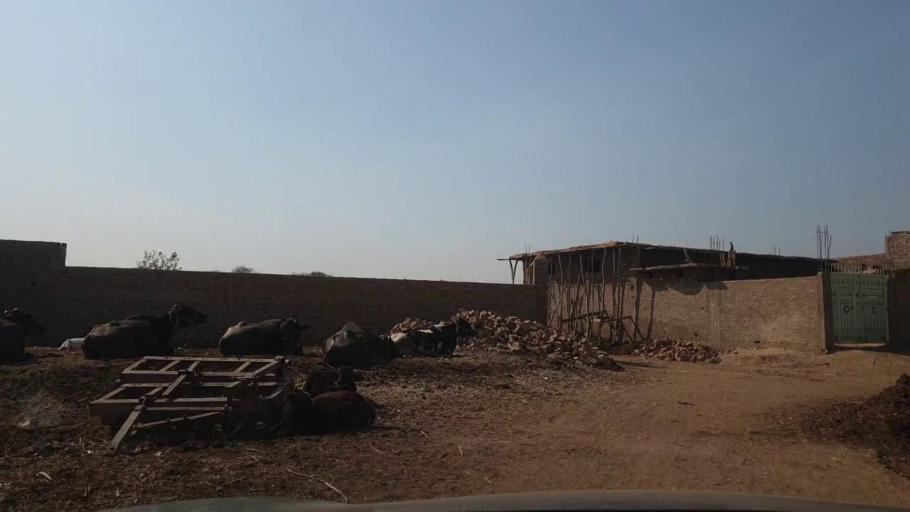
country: PK
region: Sindh
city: Tando Allahyar
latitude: 25.6024
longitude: 68.7202
